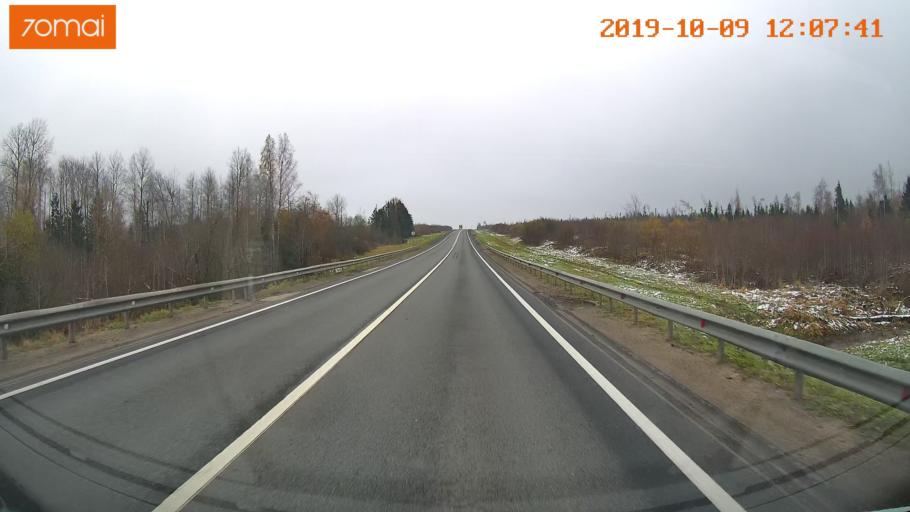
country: RU
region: Jaroslavl
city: Prechistoye
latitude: 58.5961
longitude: 40.3434
